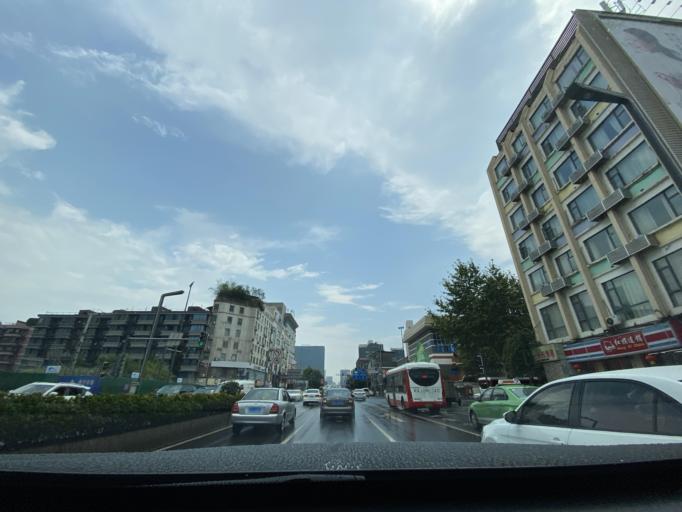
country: CN
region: Sichuan
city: Chengdu
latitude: 30.6393
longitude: 104.0735
